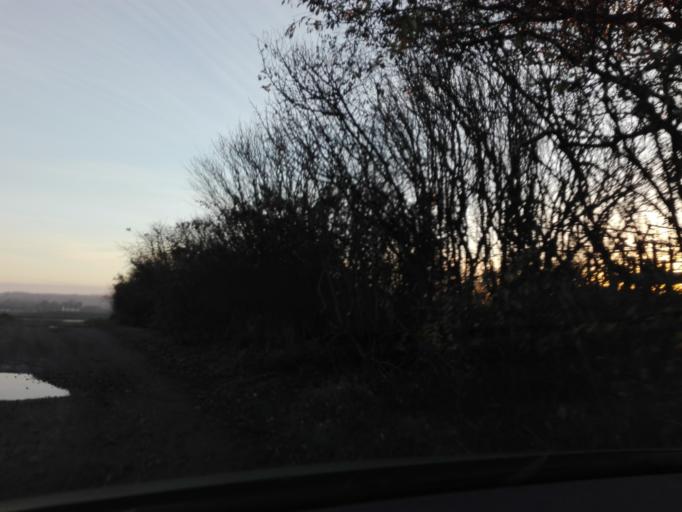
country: DK
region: Central Jutland
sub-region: Arhus Kommune
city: Framlev
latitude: 56.1425
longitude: 10.0100
